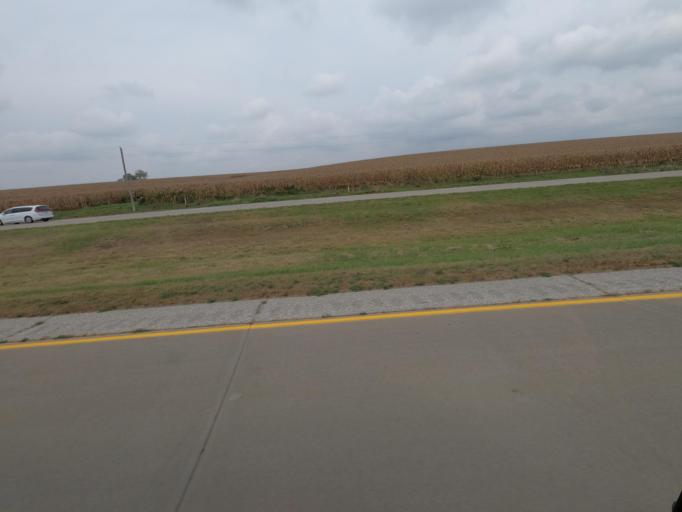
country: US
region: Iowa
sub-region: Wapello County
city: Eddyville
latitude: 41.1365
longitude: -92.5868
